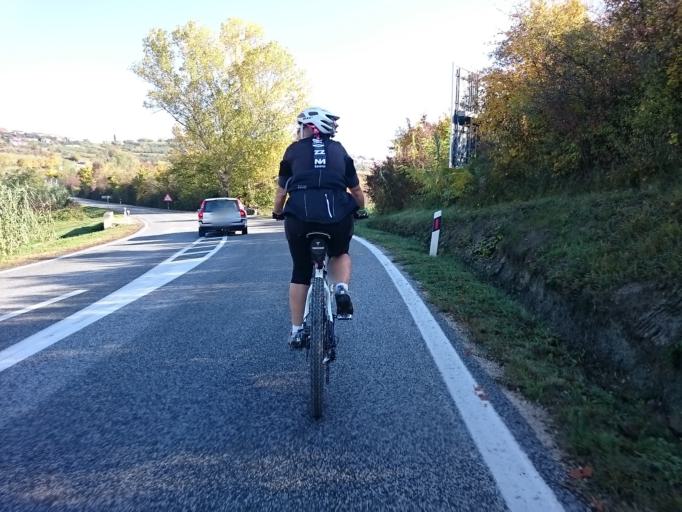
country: HR
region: Istarska
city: Buje
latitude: 45.4027
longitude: 13.6405
